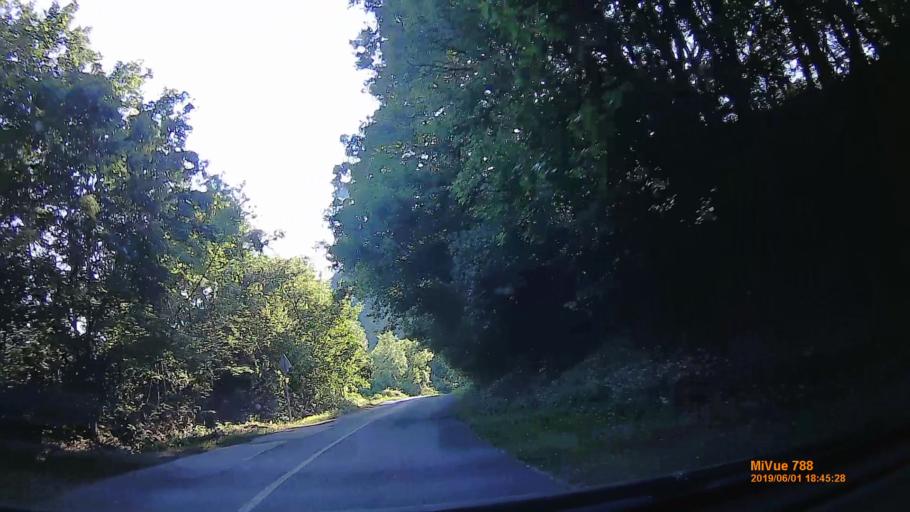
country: HU
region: Pest
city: Pilisszanto
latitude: 47.6767
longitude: 18.8950
